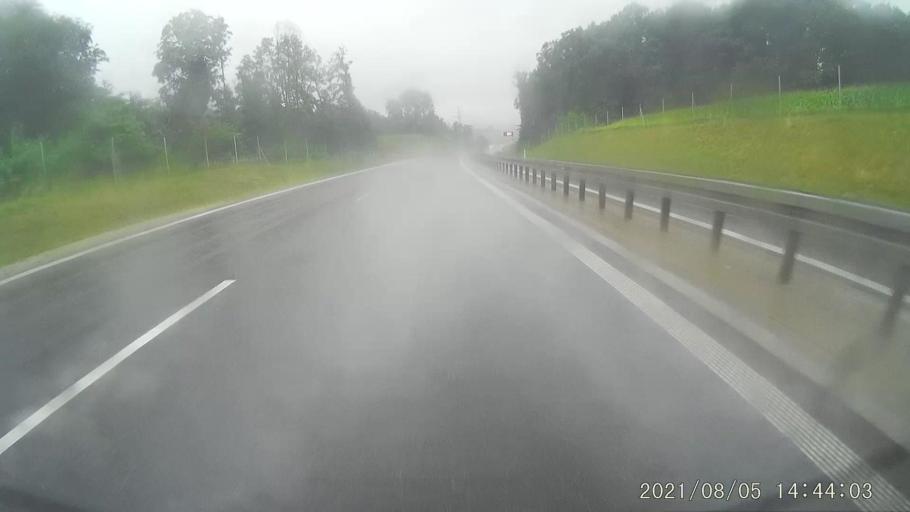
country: PL
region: Opole Voivodeship
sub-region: Powiat nyski
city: Nysa
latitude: 50.4908
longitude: 17.3845
